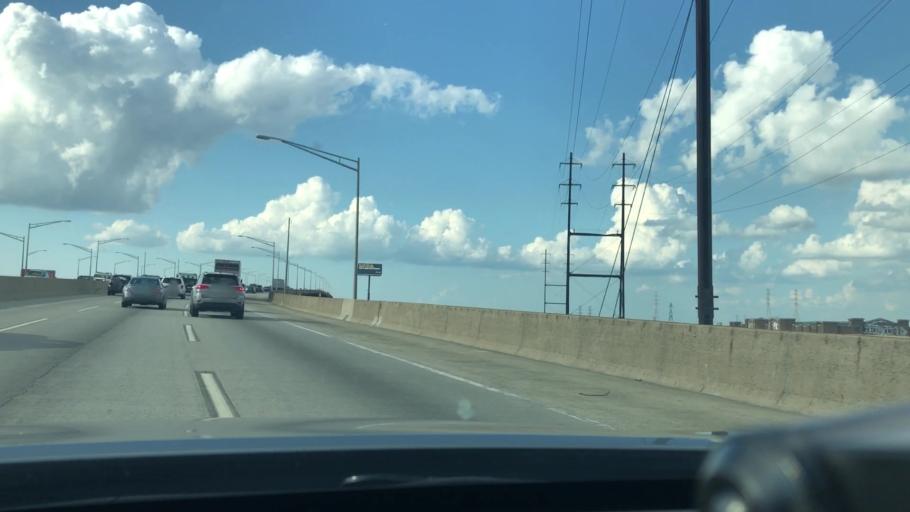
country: US
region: New Jersey
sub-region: Hudson County
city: Kearny
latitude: 40.7442
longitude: -74.1190
